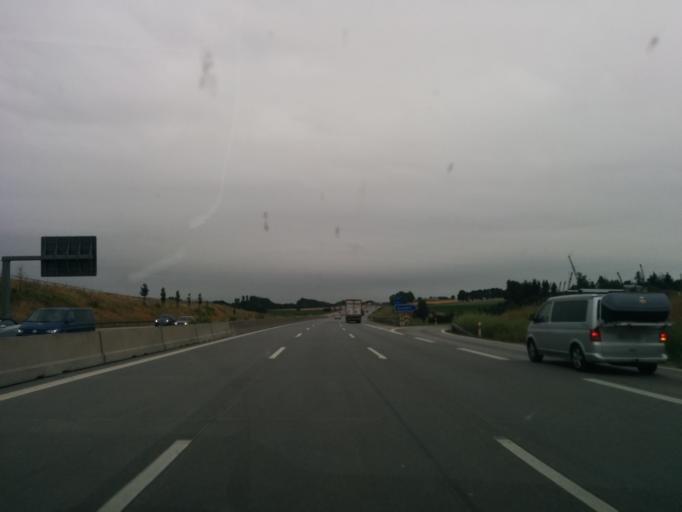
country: DE
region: Bavaria
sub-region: Swabia
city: Dasing
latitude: 48.3929
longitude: 11.0673
